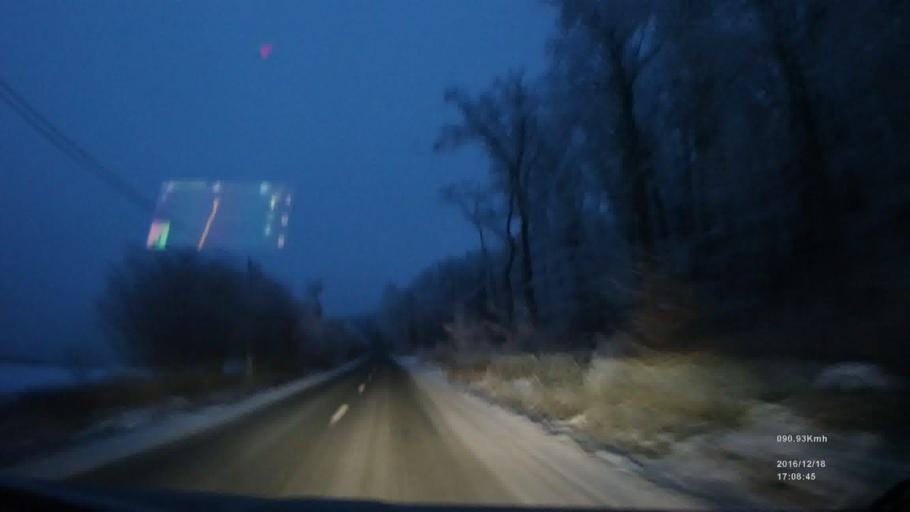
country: SK
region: Presovsky
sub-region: Okres Presov
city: Presov
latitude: 48.8815
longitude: 21.3122
